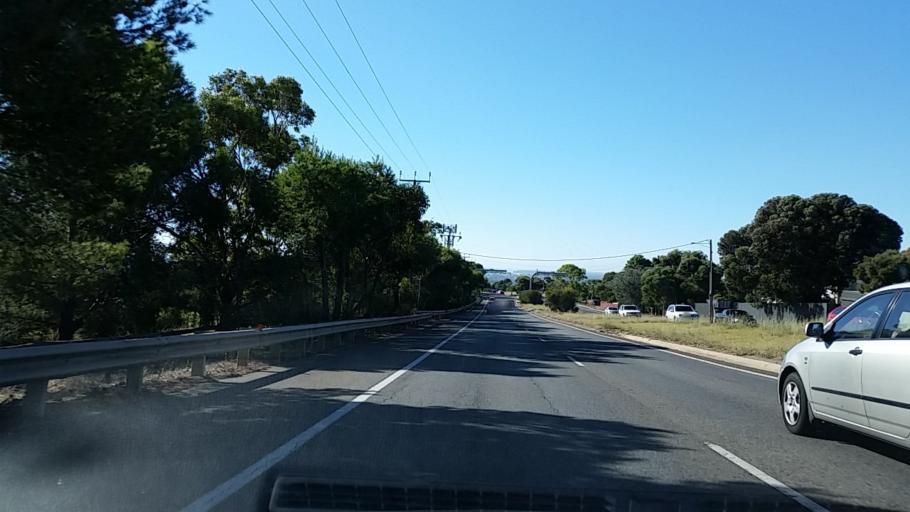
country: AU
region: South Australia
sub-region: Adelaide Hills
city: Seacliff
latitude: -35.0460
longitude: 138.5316
